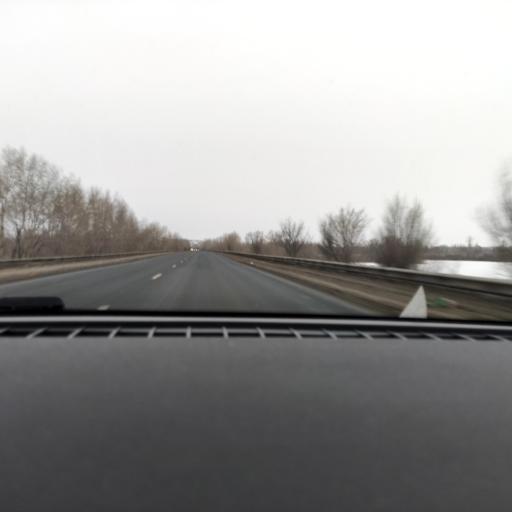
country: RU
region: Samara
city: Smyshlyayevka
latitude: 53.2106
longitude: 50.5058
